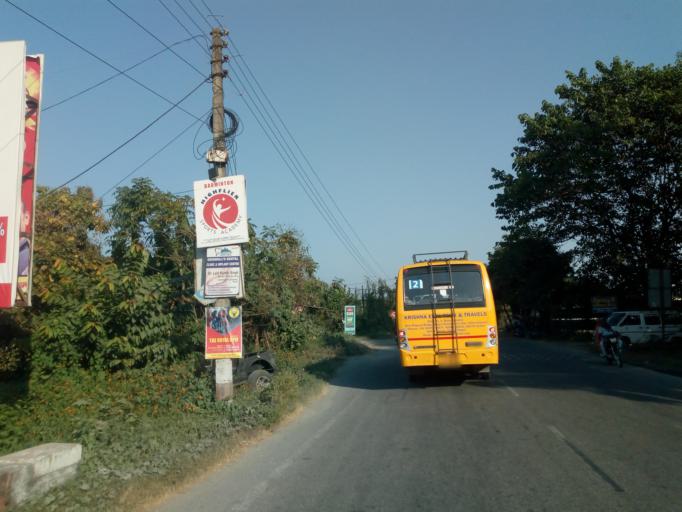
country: IN
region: Uttarakhand
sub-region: Dehradun
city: Dehradun
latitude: 30.3449
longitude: 77.9090
